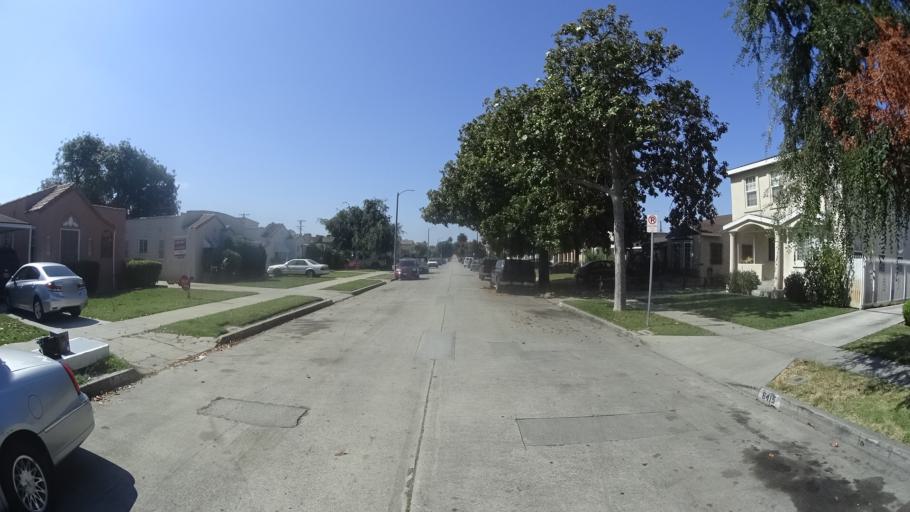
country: US
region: California
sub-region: Los Angeles County
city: View Park-Windsor Hills
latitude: 33.9815
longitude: -118.3197
